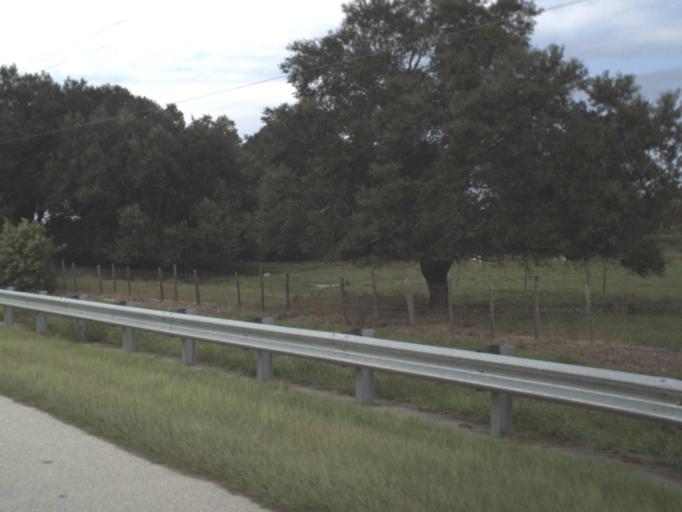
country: US
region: Florida
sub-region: Hendry County
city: Port LaBelle
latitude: 26.7684
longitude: -81.2465
